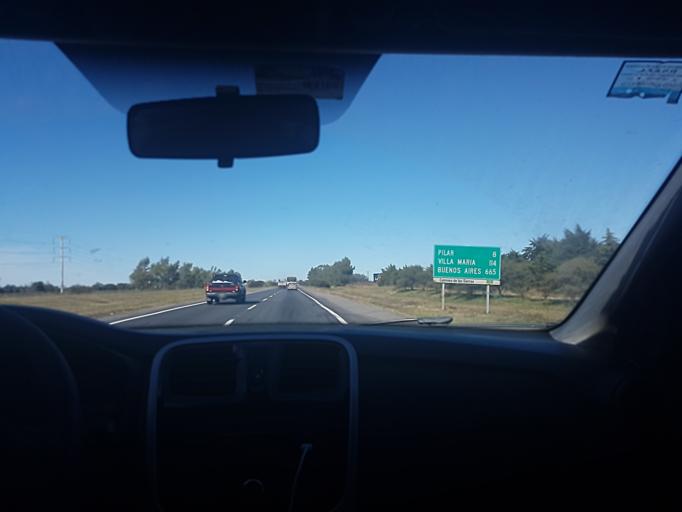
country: AR
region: Cordoba
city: Pilar
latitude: -31.6392
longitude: -63.8676
